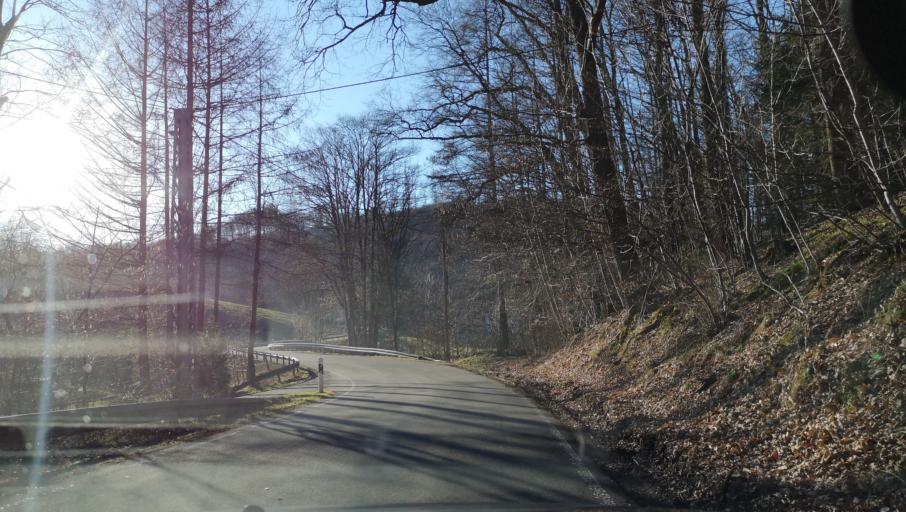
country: DE
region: North Rhine-Westphalia
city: Ennepetal
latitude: 51.2743
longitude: 7.4021
